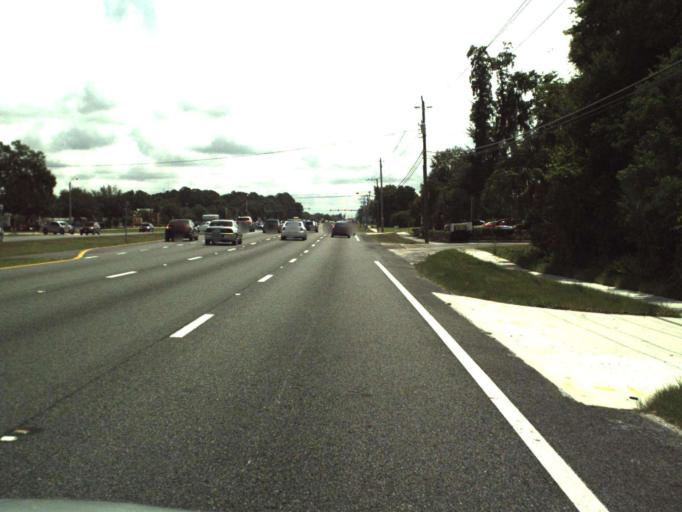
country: US
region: Florida
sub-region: Seminole County
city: Lake Mary
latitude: 28.8114
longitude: -81.3284
